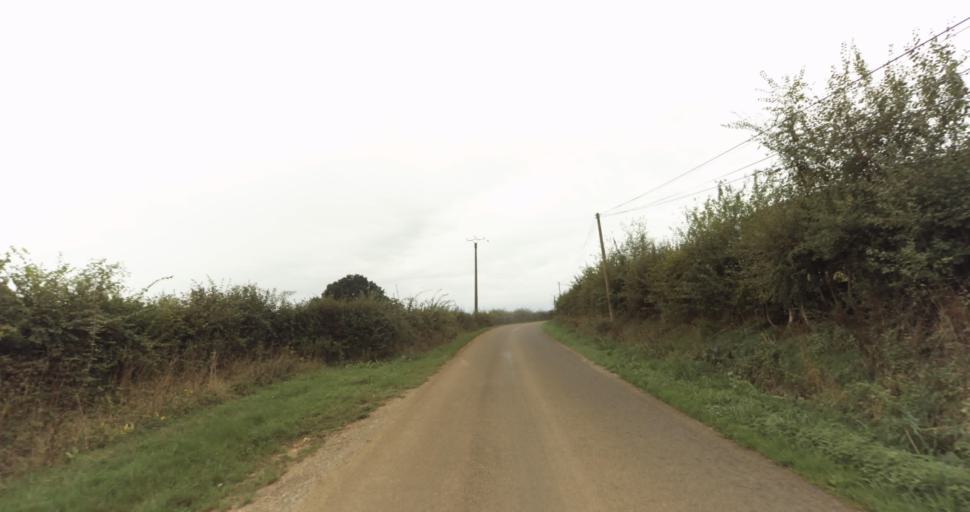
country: FR
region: Lower Normandy
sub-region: Departement de l'Orne
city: Gace
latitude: 48.7615
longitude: 0.3308
